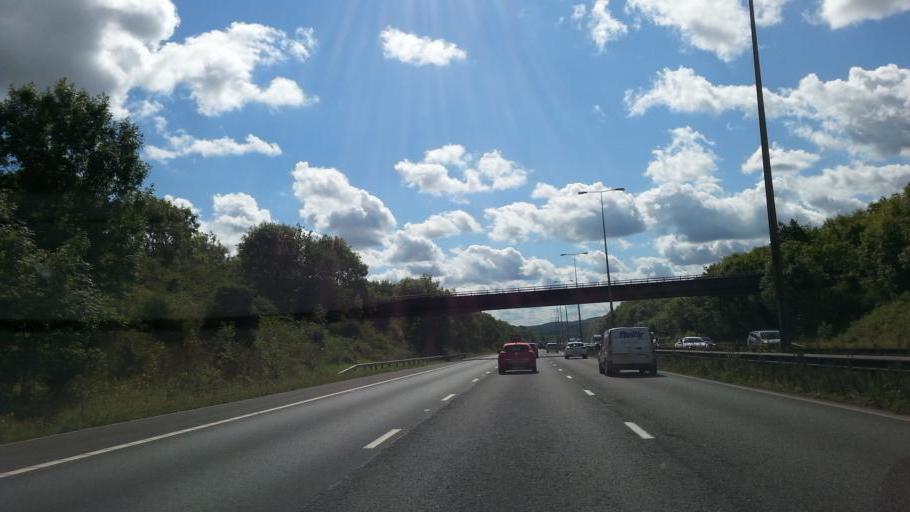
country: GB
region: England
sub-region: Leicestershire
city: Shepshed
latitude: 52.7920
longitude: -1.2904
